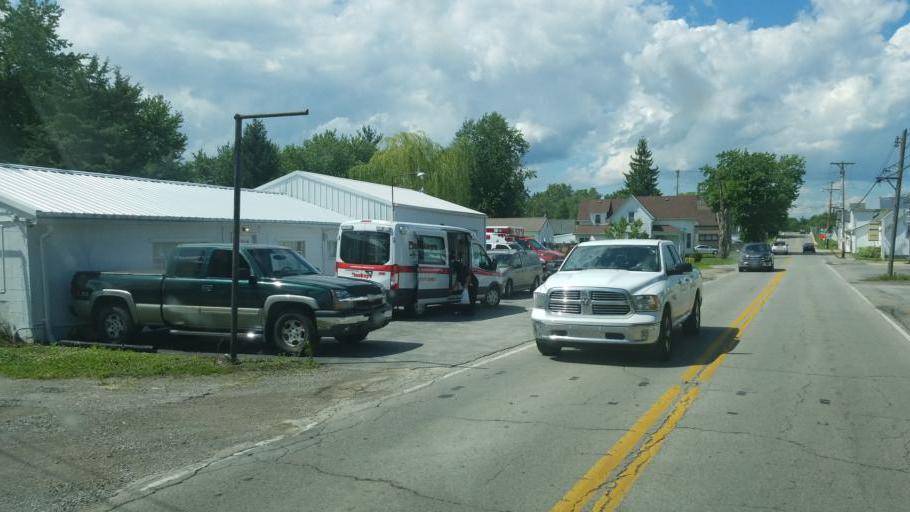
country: US
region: Ohio
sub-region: Highland County
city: Greenfield
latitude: 39.3439
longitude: -83.3902
